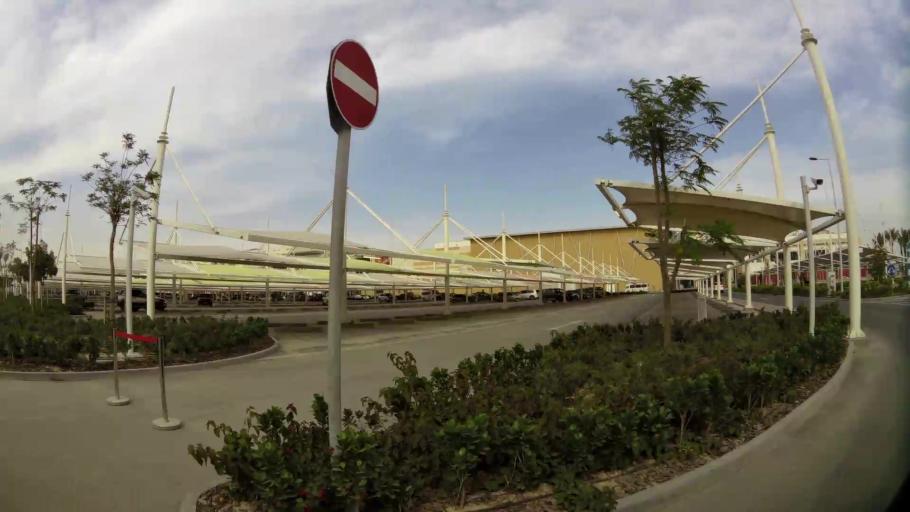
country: QA
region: Baladiyat ar Rayyan
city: Ar Rayyan
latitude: 25.3252
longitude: 51.3474
